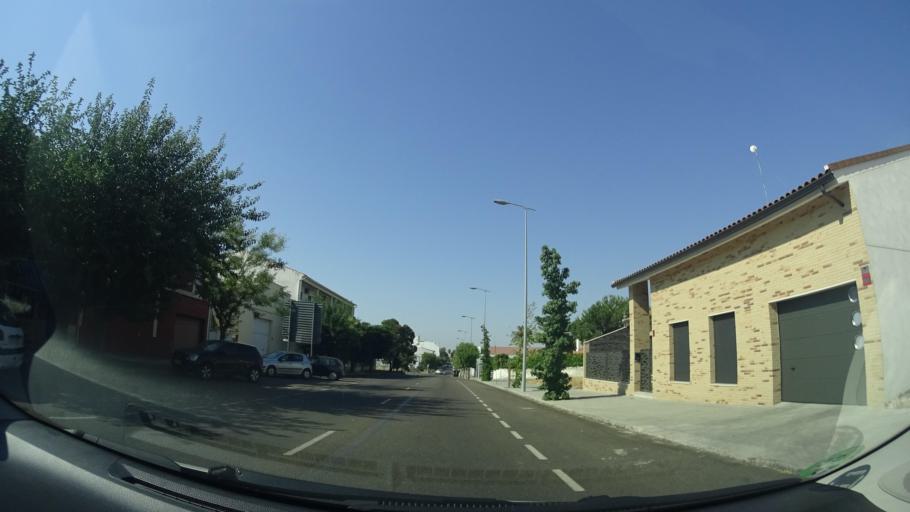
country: ES
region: Extremadura
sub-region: Provincia de Caceres
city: Miajadas
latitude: 39.1587
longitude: -5.8994
